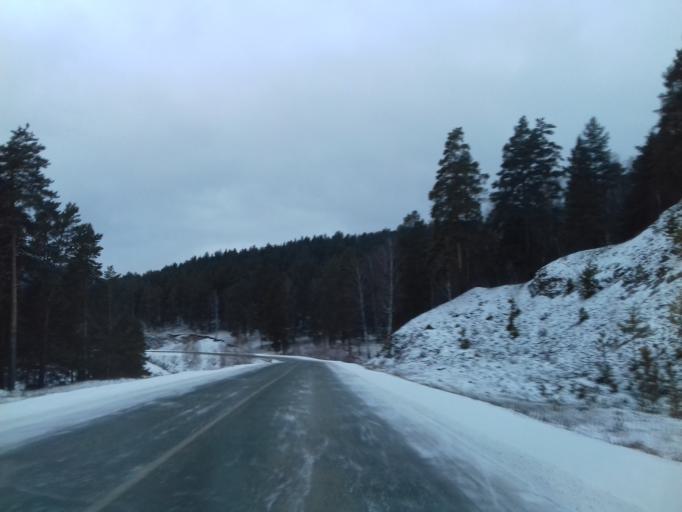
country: RU
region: Bashkortostan
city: Starosubkhangulovo
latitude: 53.2819
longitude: 57.5340
